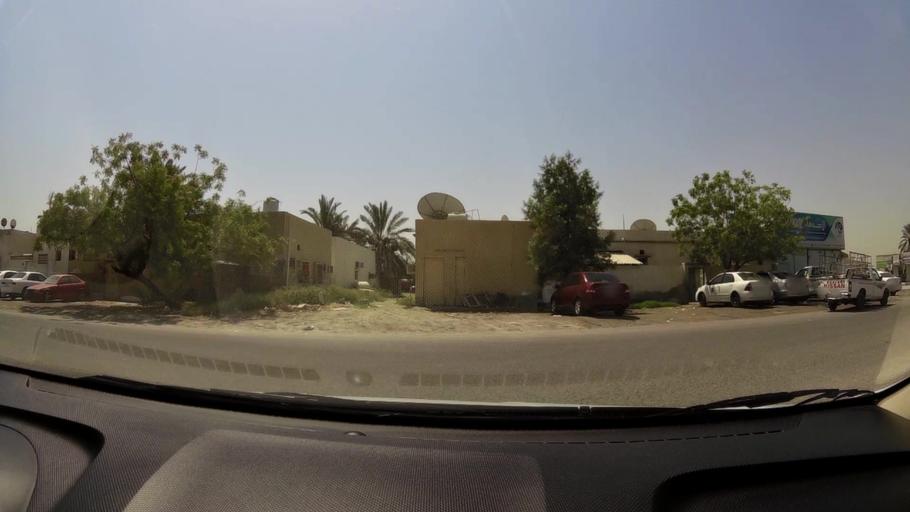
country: AE
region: Umm al Qaywayn
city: Umm al Qaywayn
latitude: 25.5522
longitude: 55.5512
